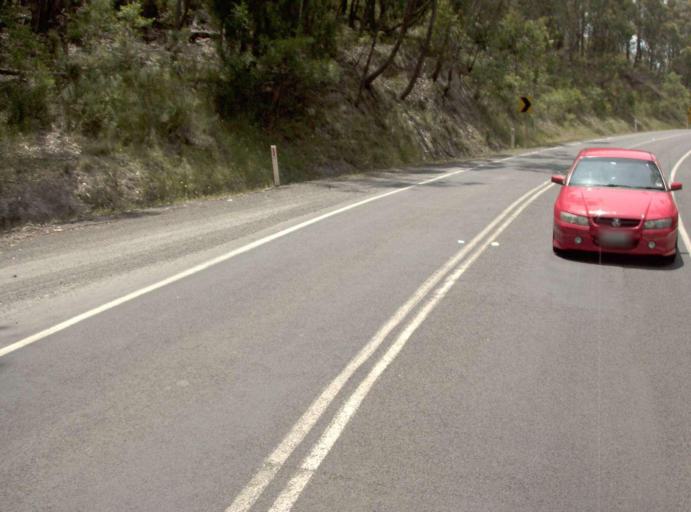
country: AU
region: Victoria
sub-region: Latrobe
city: Traralgon
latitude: -38.3832
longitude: 146.7571
